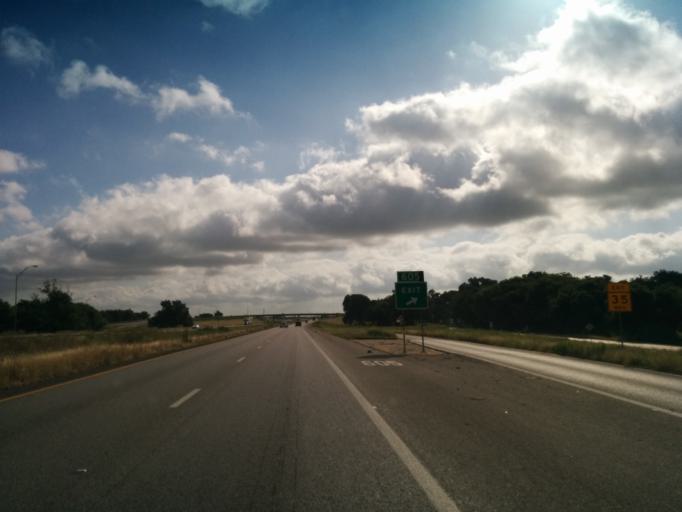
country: US
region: Texas
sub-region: Guadalupe County
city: McQueeney
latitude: 29.5683
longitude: -98.0203
